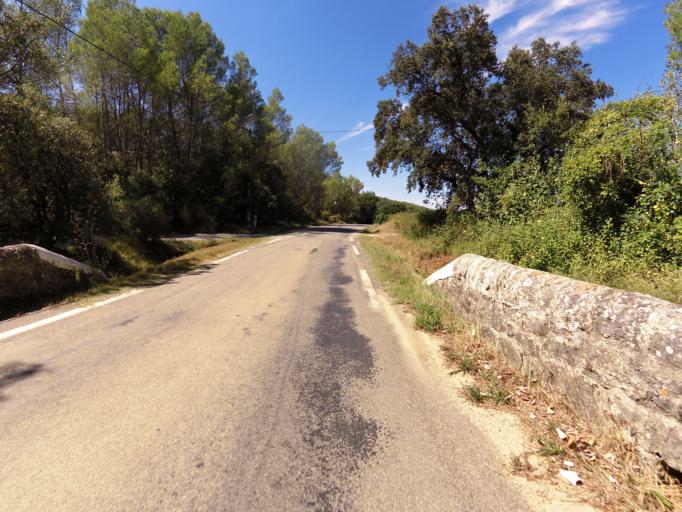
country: FR
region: Languedoc-Roussillon
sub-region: Departement du Gard
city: Quissac
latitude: 43.8555
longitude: 4.0457
